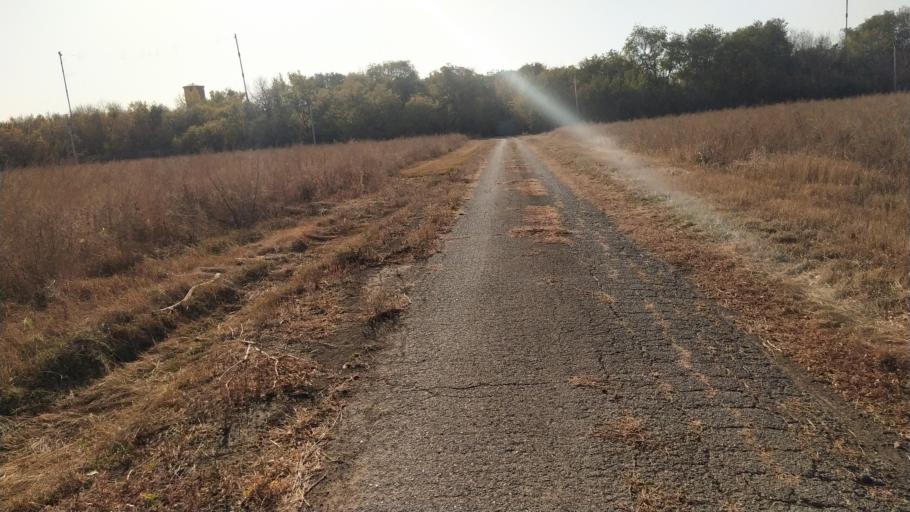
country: RU
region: Rostov
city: Bataysk
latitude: 47.1042
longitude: 39.6685
